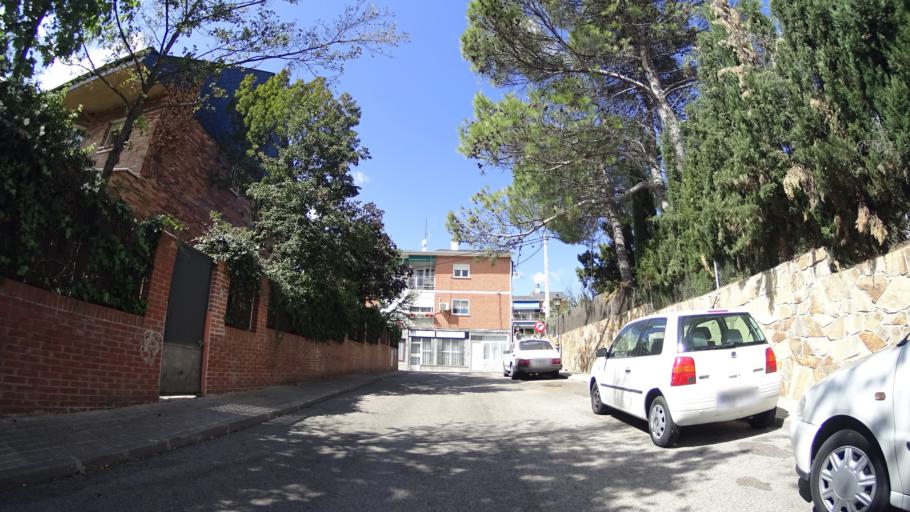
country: ES
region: Madrid
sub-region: Provincia de Madrid
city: Torrelodones
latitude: 40.5773
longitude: -3.9552
